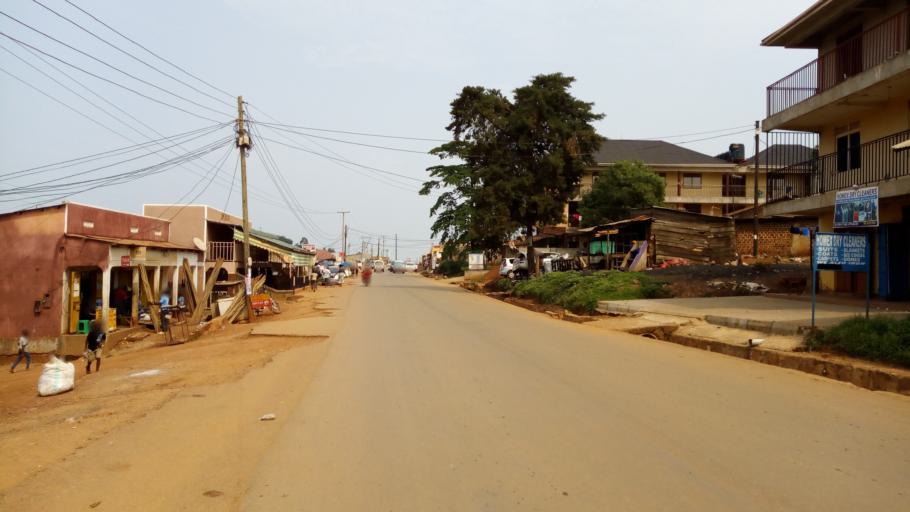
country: UG
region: Central Region
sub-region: Wakiso District
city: Kireka
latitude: 0.3122
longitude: 32.6516
